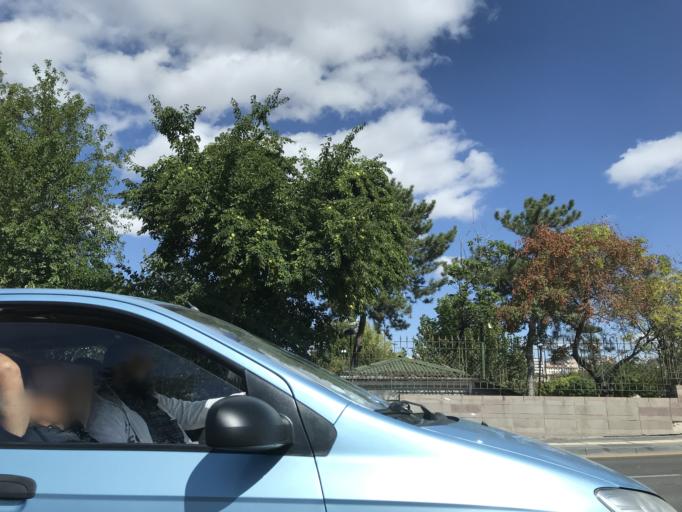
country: TR
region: Ankara
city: Ankara
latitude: 39.9347
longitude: 32.8512
